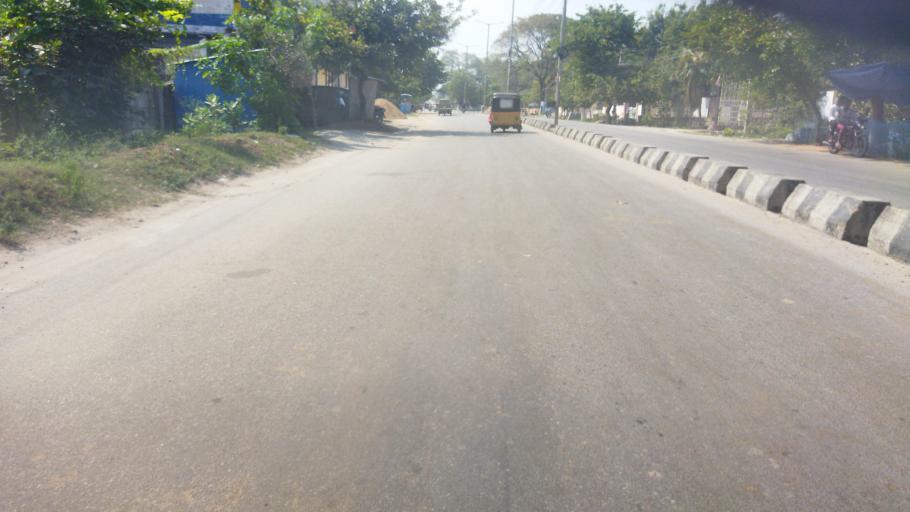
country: IN
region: Telangana
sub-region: Nalgonda
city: Nalgonda
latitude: 17.0709
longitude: 79.2837
